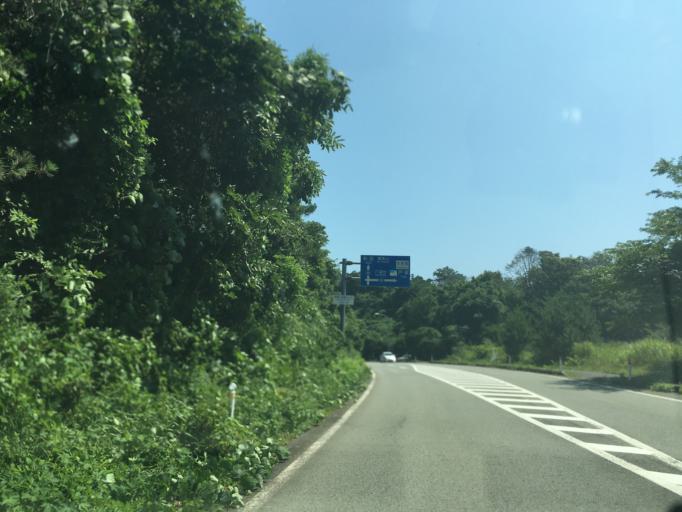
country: JP
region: Akita
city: Tenno
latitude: 39.9733
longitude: 139.7387
